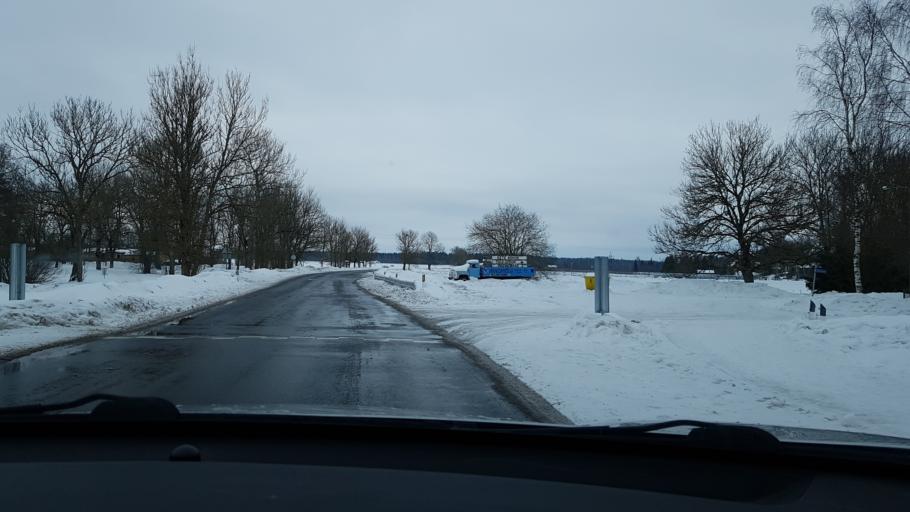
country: EE
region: Jaervamaa
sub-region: Jaerva-Jaani vald
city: Jarva-Jaani
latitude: 59.1409
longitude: 25.7527
